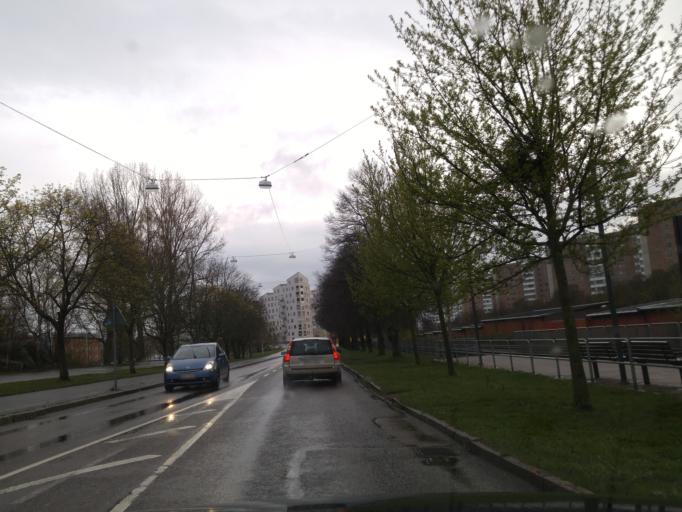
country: SE
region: Vaestra Goetaland
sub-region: Goteborg
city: Majorna
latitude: 57.6566
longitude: 11.9177
